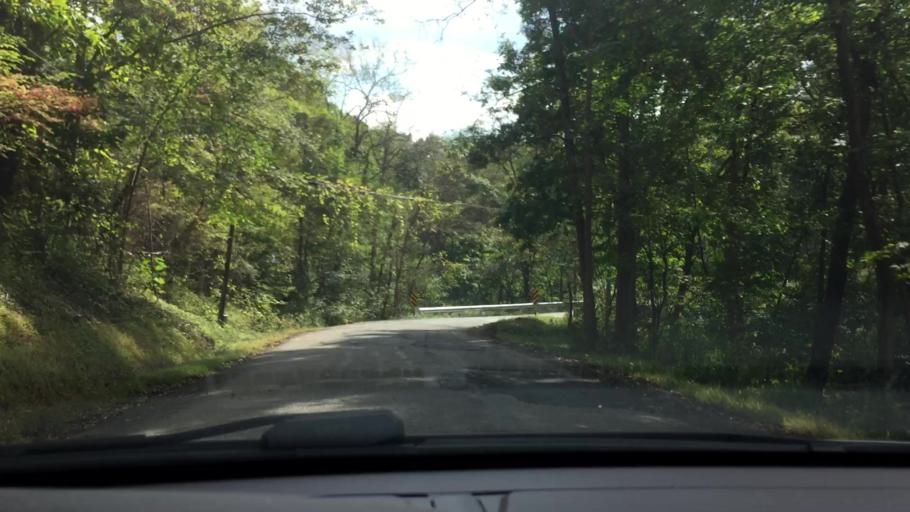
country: US
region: Pennsylvania
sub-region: Washington County
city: Thompsonville
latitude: 40.2978
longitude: -80.1439
